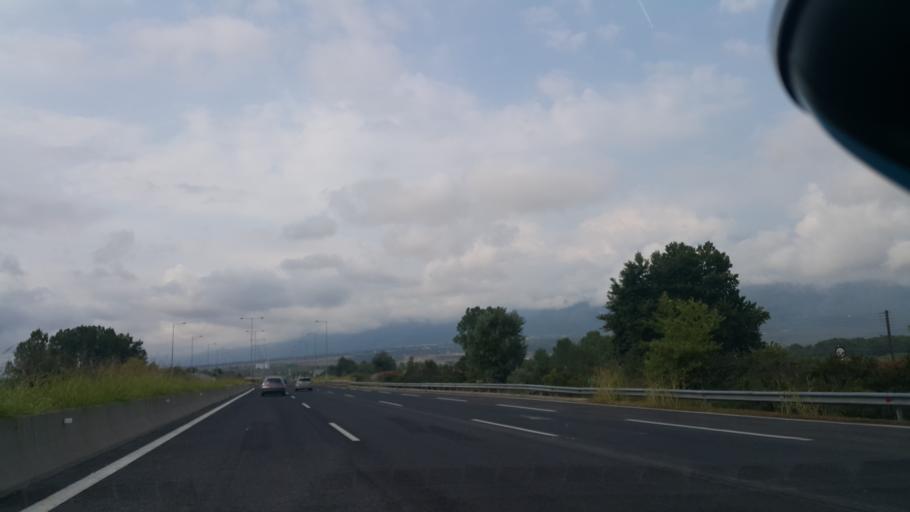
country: GR
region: Central Macedonia
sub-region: Nomos Pierias
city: Dion
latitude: 40.1571
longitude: 22.5434
